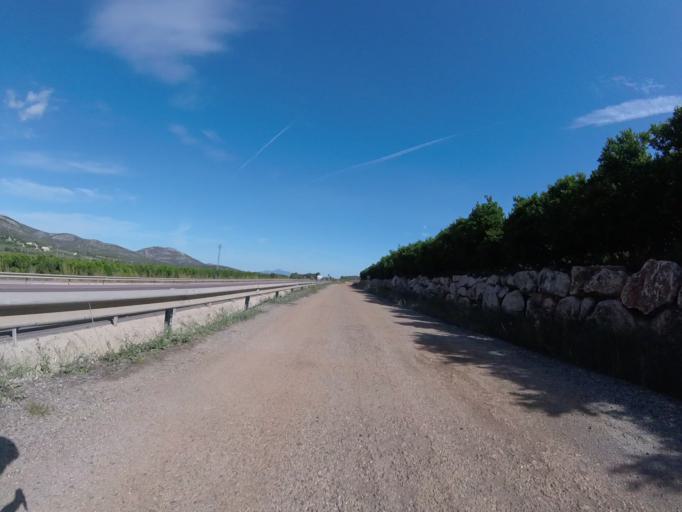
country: ES
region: Valencia
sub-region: Provincia de Castello
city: Santa Magdalena de Pulpis
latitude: 40.3760
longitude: 0.3307
